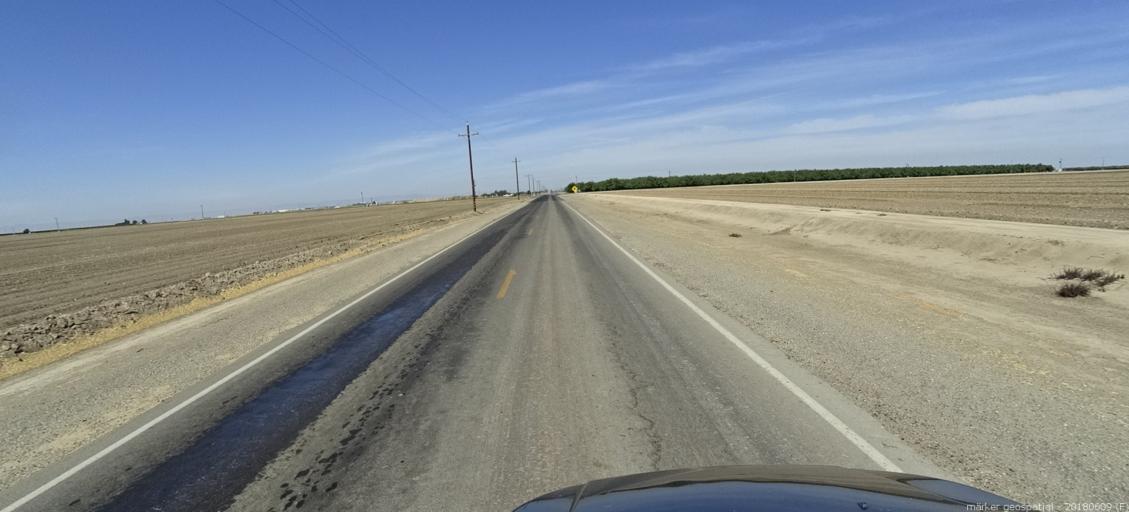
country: US
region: California
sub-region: Madera County
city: Fairmead
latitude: 36.9528
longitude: -120.2520
